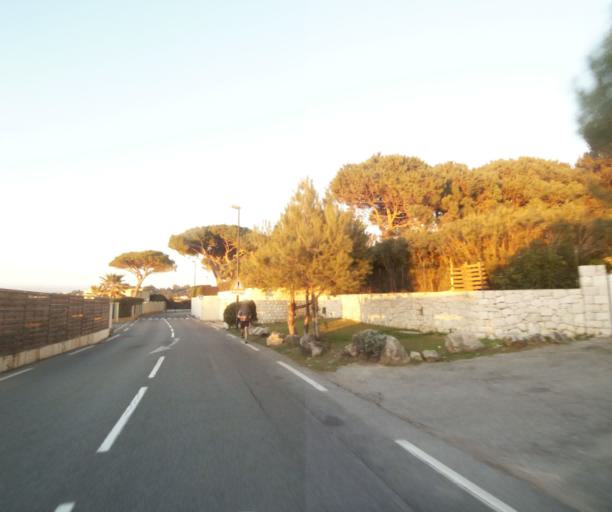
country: FR
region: Provence-Alpes-Cote d'Azur
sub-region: Departement des Alpes-Maritimes
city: Antibes
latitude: 43.5501
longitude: 7.1187
